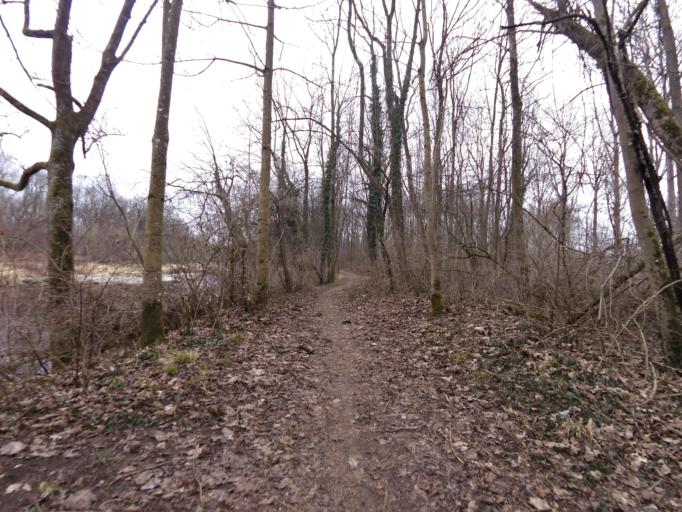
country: DE
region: Bavaria
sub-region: Upper Bavaria
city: Wang
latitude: 48.4975
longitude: 11.9517
